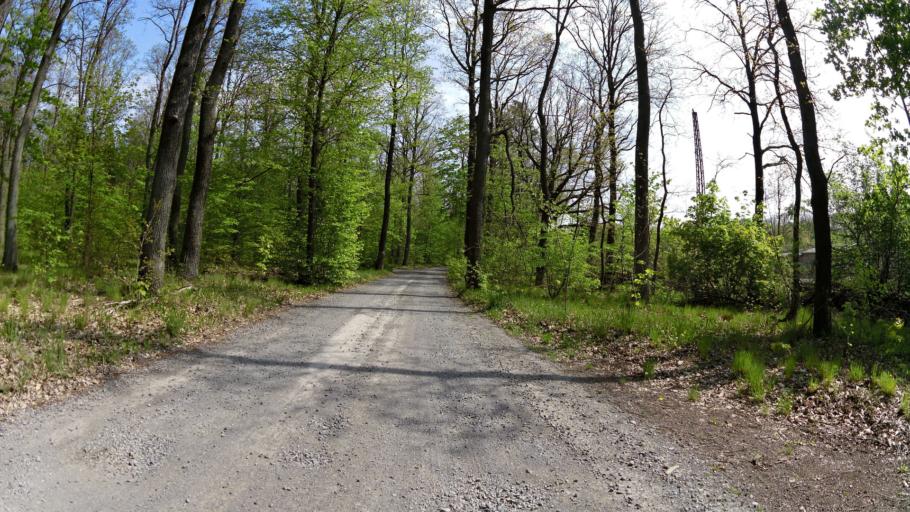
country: DE
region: Brandenburg
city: Spreenhagen
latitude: 52.3999
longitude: 13.9241
